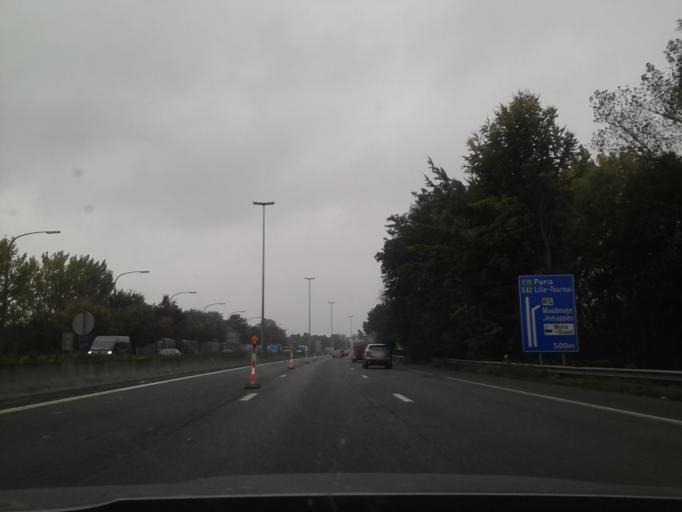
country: BE
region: Wallonia
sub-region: Province du Hainaut
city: Mons
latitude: 50.4675
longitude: 3.9328
